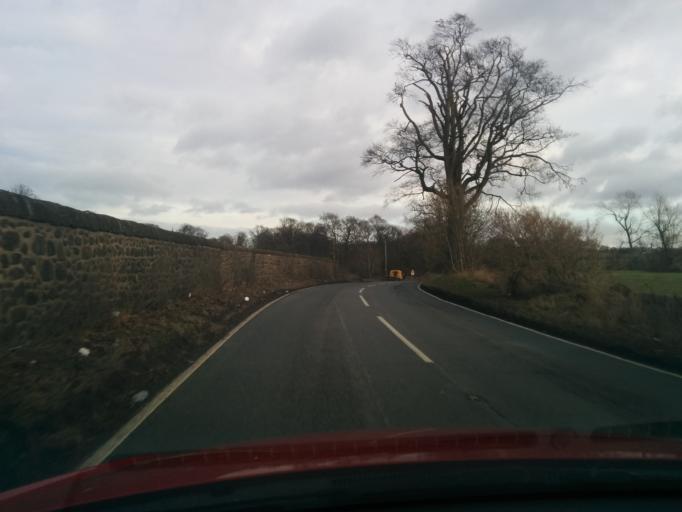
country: GB
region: Scotland
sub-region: Fife
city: Limekilns
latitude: 55.9846
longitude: -3.5187
